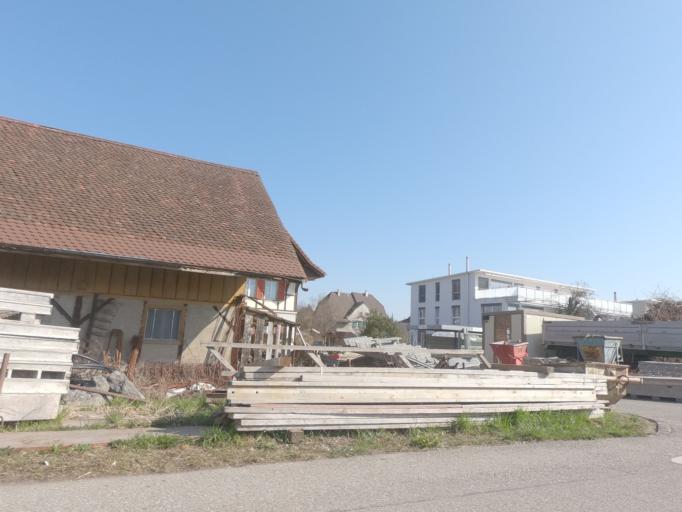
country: CH
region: Solothurn
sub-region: Bezirk Wasseramt
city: Derendingen
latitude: 47.2021
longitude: 7.5852
